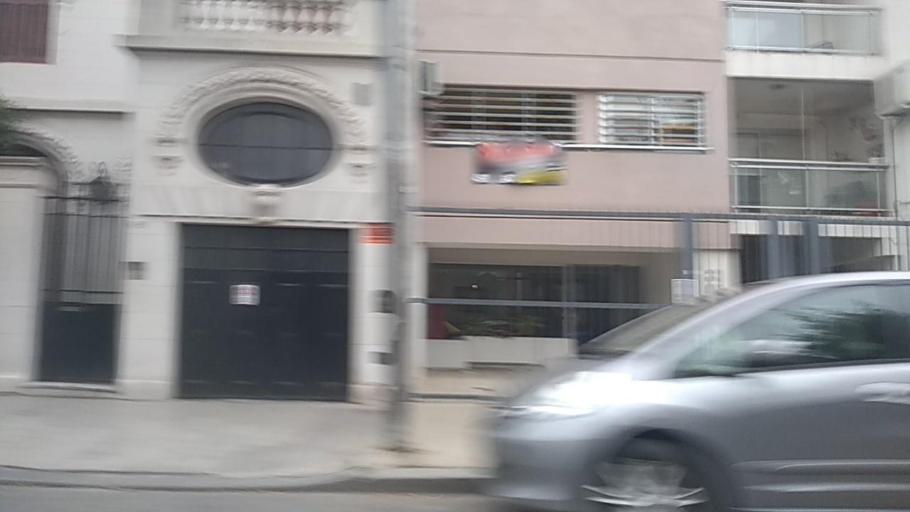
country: AR
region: Buenos Aires F.D.
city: Villa Santa Rita
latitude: -34.5985
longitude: -58.4949
